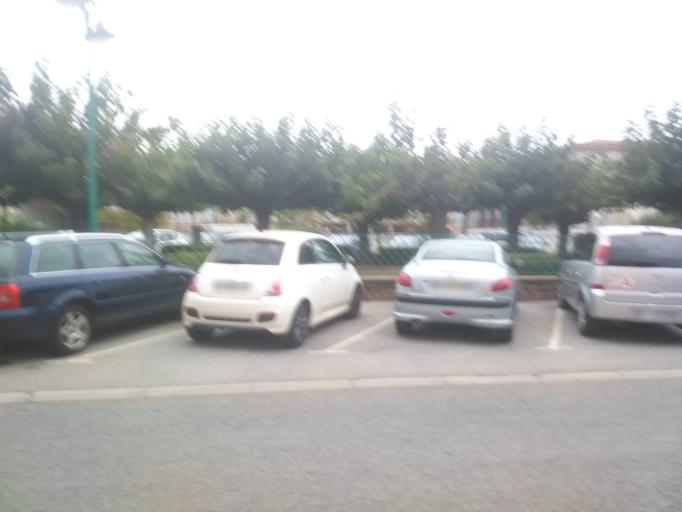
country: FR
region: Provence-Alpes-Cote d'Azur
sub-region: Departement du Var
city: Le Muy
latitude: 43.4725
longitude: 6.5647
